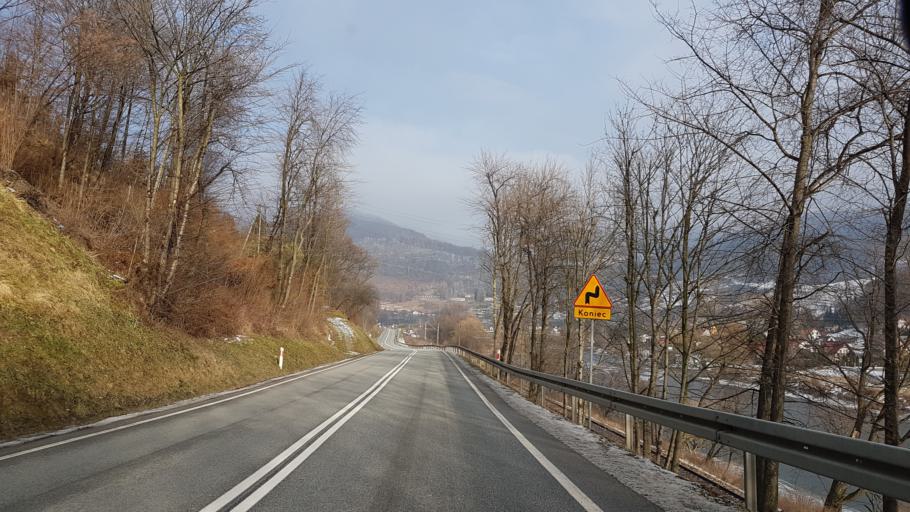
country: PL
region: Lesser Poland Voivodeship
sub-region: Powiat nowosadecki
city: Piwniczna-Zdroj
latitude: 49.4607
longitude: 20.6951
